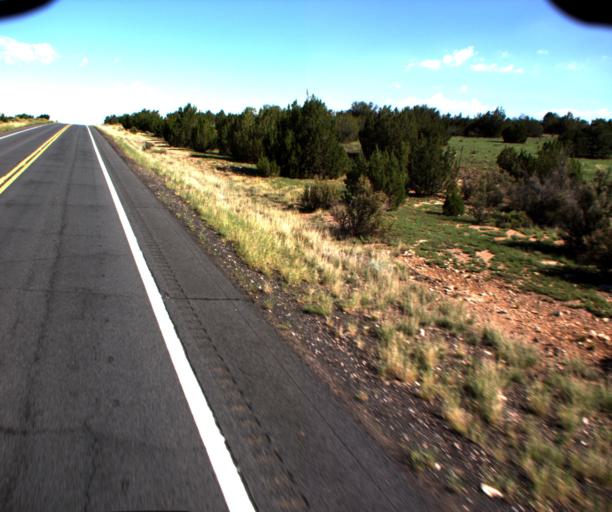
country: US
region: Arizona
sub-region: Coconino County
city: Williams
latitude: 35.4717
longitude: -112.1755
